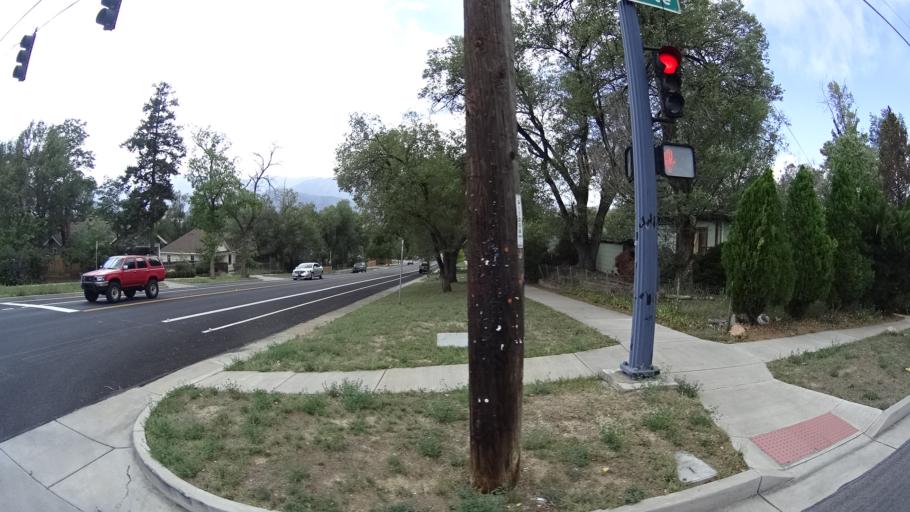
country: US
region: Colorado
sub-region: El Paso County
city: Colorado Springs
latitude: 38.8279
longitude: -104.8083
